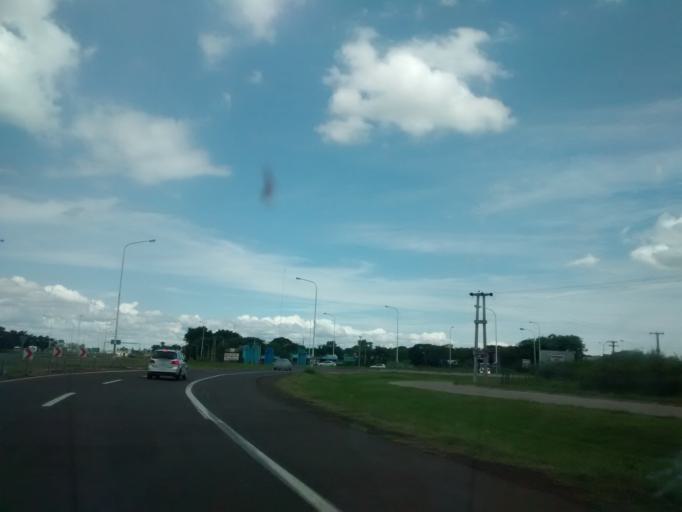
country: AR
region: Chaco
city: Resistencia
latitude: -27.4144
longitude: -58.9701
